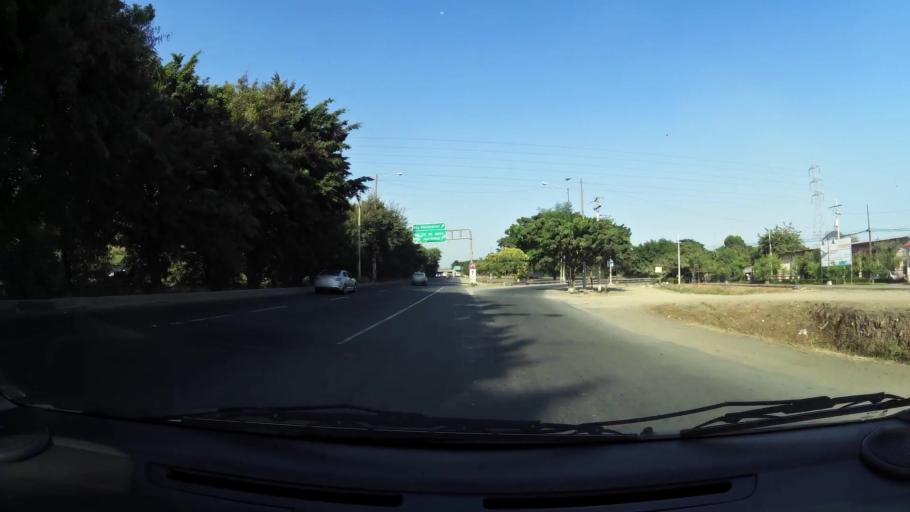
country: EC
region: Guayas
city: Santa Lucia
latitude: -2.1872
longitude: -79.9594
